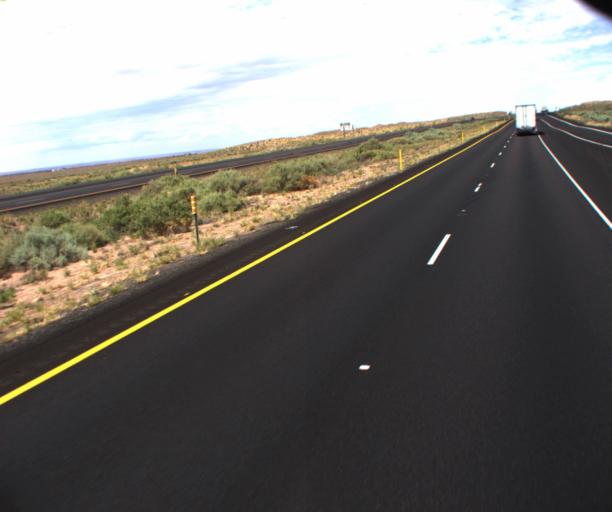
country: US
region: Arizona
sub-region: Navajo County
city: Holbrook
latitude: 34.9913
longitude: -109.9644
